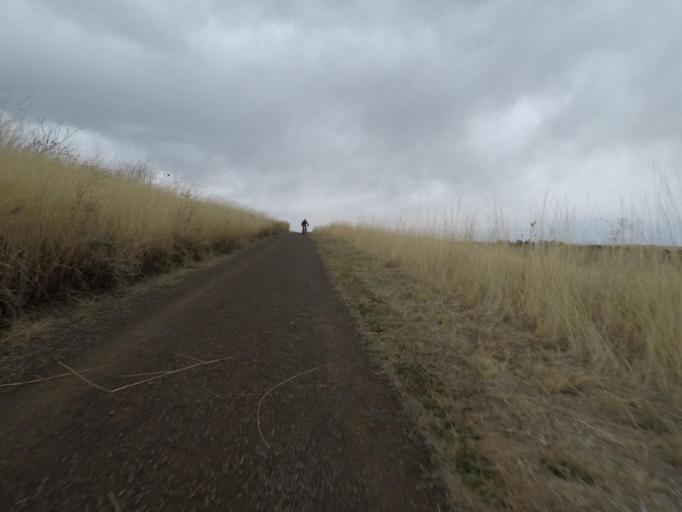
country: US
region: Washington
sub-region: Walla Walla County
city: Walla Walla East
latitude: 46.0602
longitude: -118.2597
